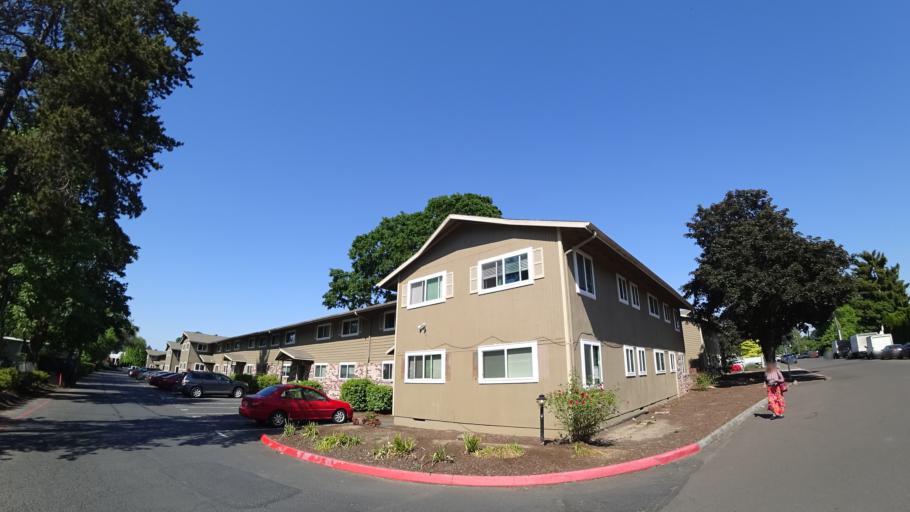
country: US
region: Oregon
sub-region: Washington County
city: Beaverton
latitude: 45.4910
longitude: -122.8191
